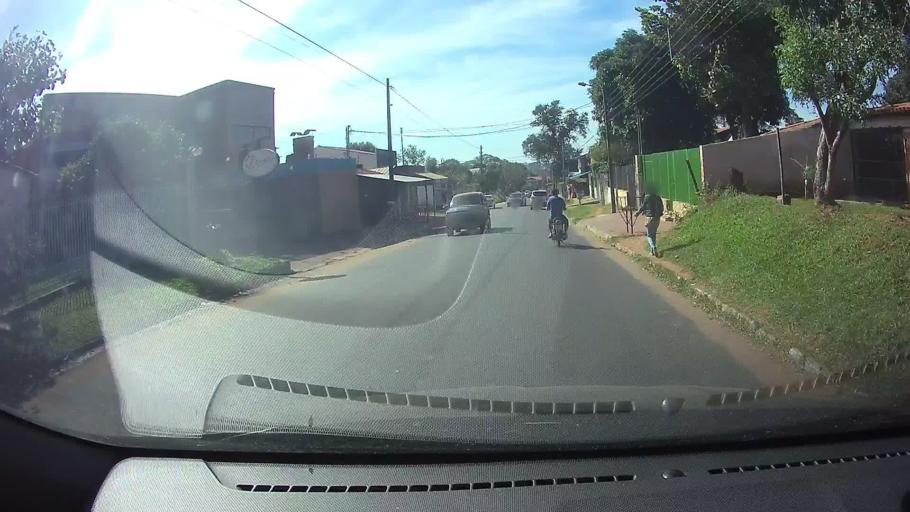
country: PY
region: Central
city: Villa Elisa
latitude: -25.3733
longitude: -57.5759
